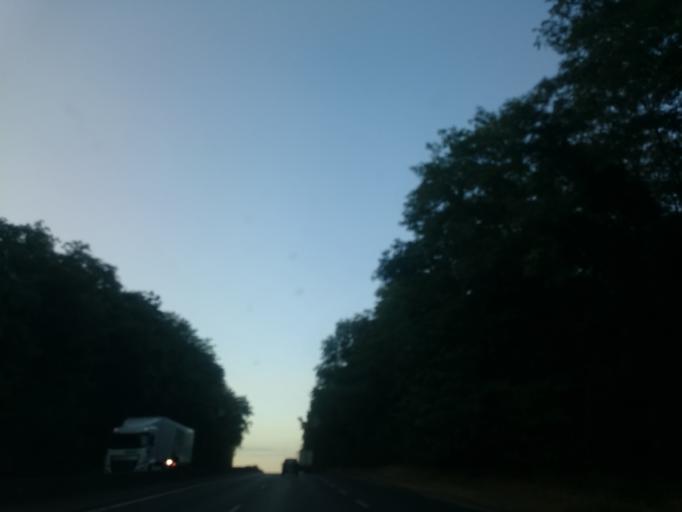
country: FR
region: Ile-de-France
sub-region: Departement de l'Essonne
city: Chamarande
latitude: 48.5142
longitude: 2.2033
